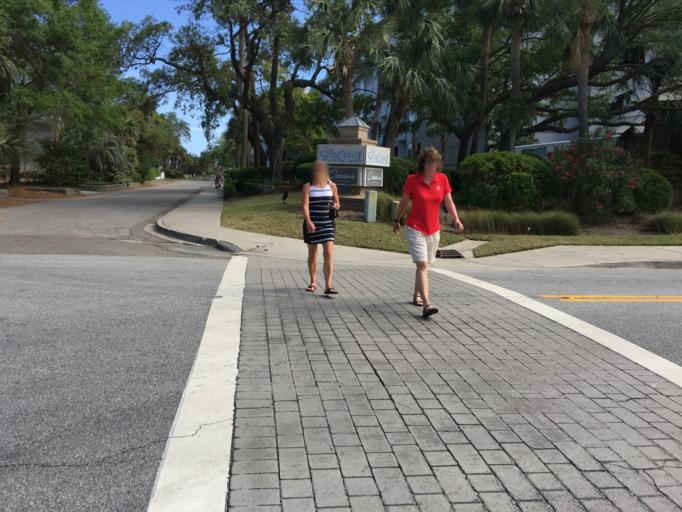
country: US
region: South Carolina
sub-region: Beaufort County
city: Hilton Head Island
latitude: 32.1435
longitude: -80.7492
